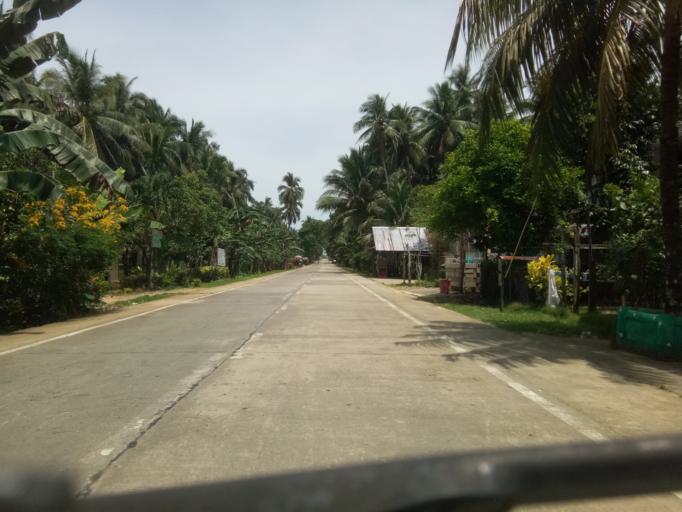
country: PH
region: Caraga
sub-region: Province of Surigao del Norte
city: Del Carmen, Surigao del Norte
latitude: 9.8730
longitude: 125.9746
